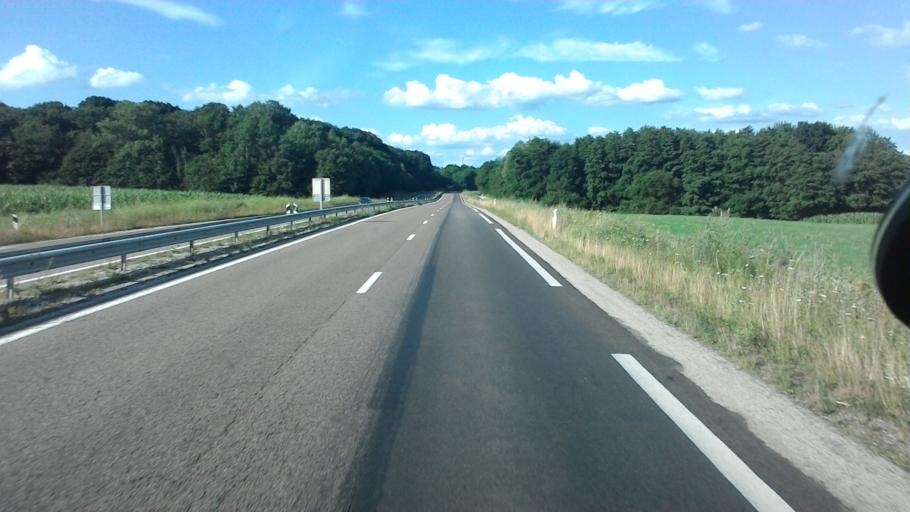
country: FR
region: Franche-Comte
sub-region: Departement de la Haute-Saone
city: Luxeuil-les-Bains
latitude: 47.7405
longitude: 6.3214
